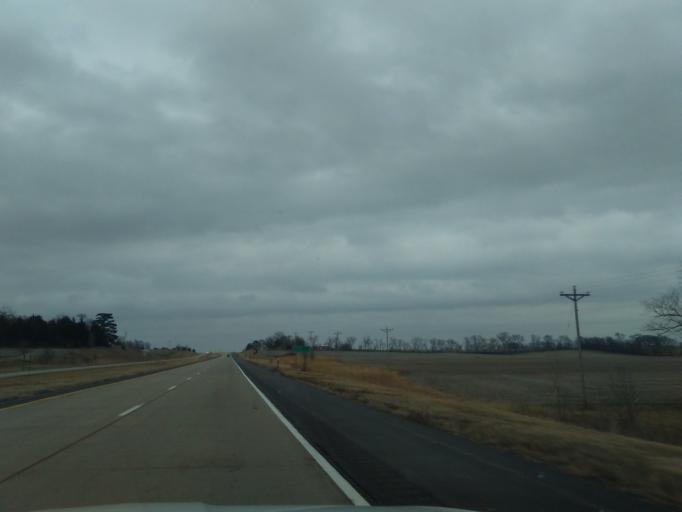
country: US
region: Nebraska
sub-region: Cass County
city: Eagle
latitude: 40.7113
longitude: -96.3862
